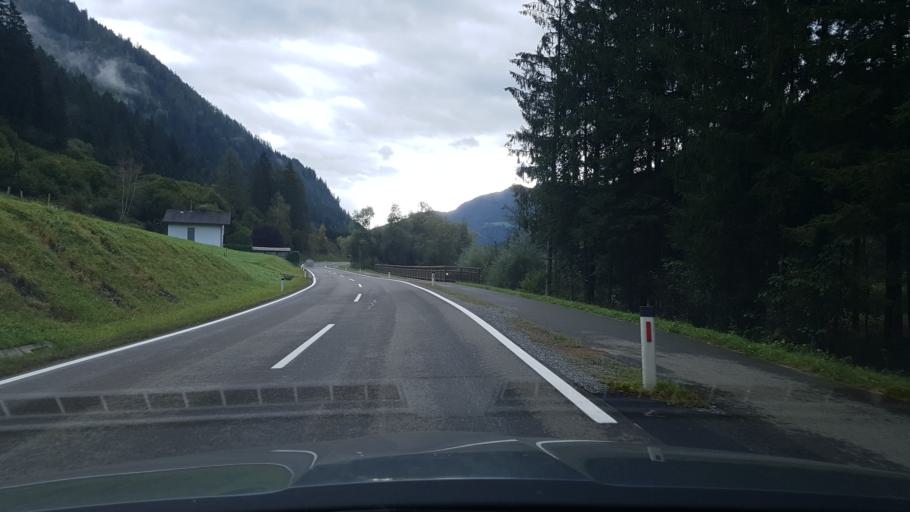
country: AT
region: Styria
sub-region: Politischer Bezirk Murau
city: Winklern bei Oberwolz
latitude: 47.1622
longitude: 14.2490
